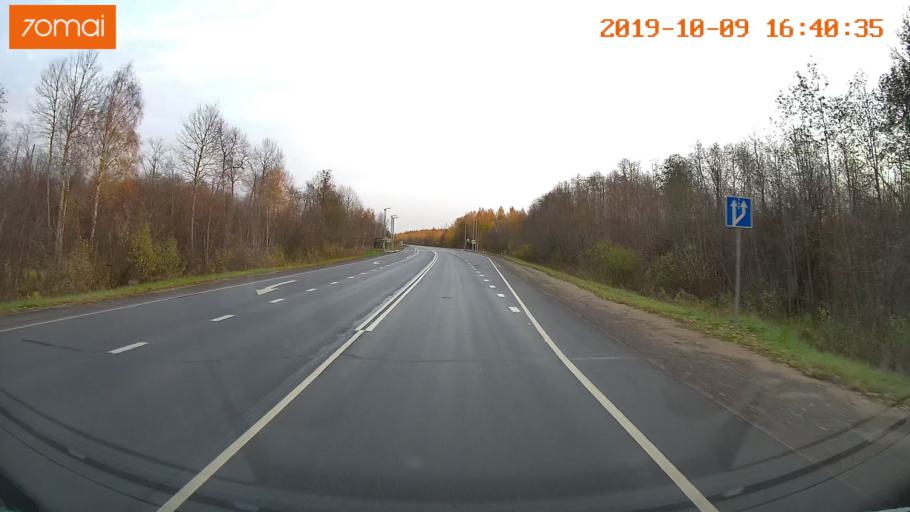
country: RU
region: Kostroma
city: Volgorechensk
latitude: 57.4818
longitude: 41.0631
